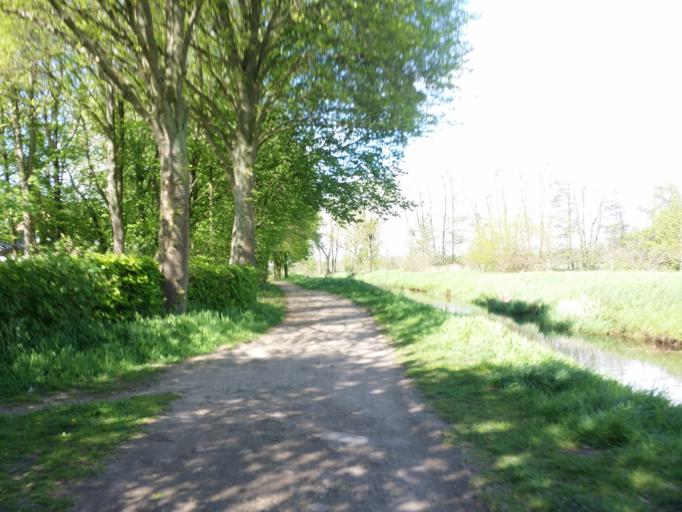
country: DE
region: Lower Saxony
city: Delmenhorst
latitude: 53.0594
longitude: 8.6751
